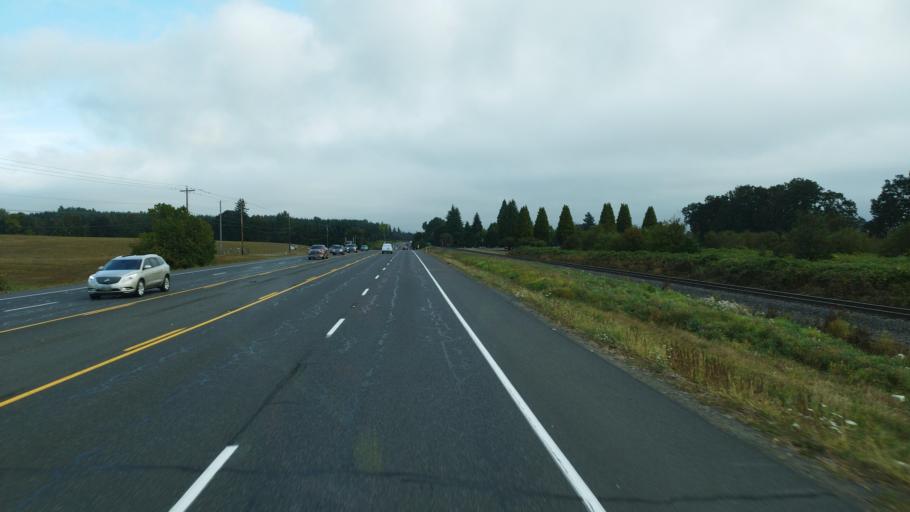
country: US
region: Oregon
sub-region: Columbia County
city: Scappoose
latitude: 45.7837
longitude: -122.8733
